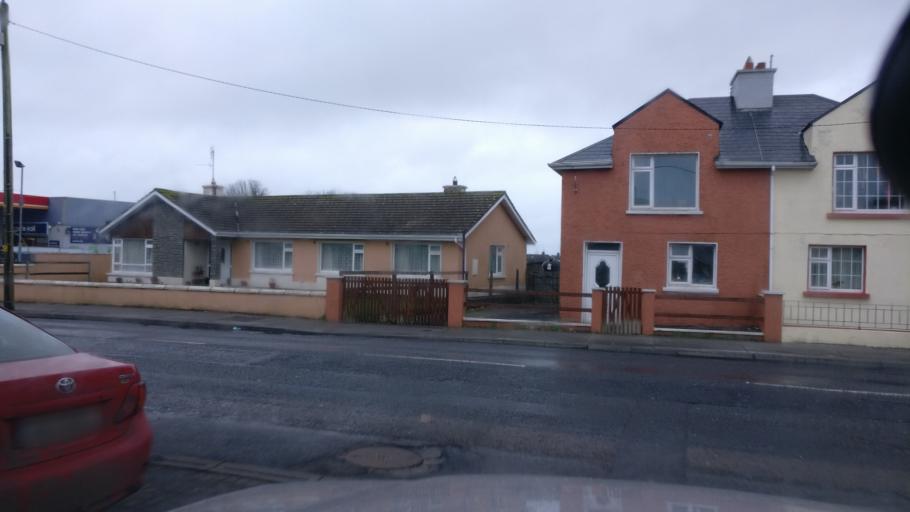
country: IE
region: Connaught
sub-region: County Galway
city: Loughrea
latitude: 53.2010
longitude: -8.5560
